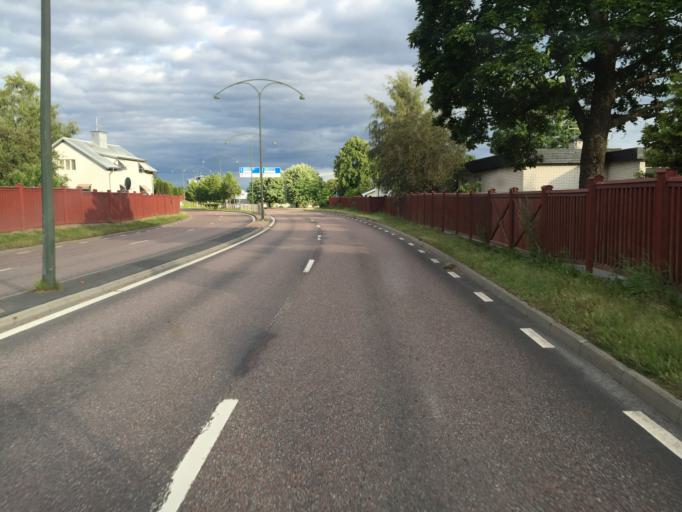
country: SE
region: Dalarna
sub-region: Borlange Kommun
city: Borlaenge
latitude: 60.4888
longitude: 15.4111
